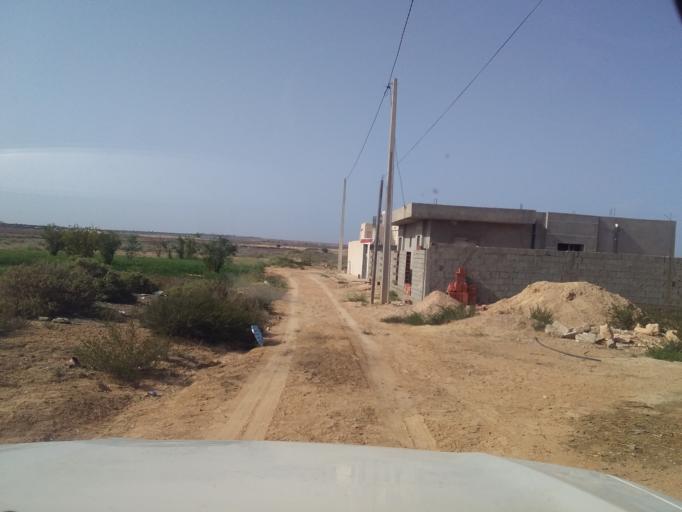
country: TN
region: Qabis
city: Gabes
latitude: 33.6429
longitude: 10.2952
